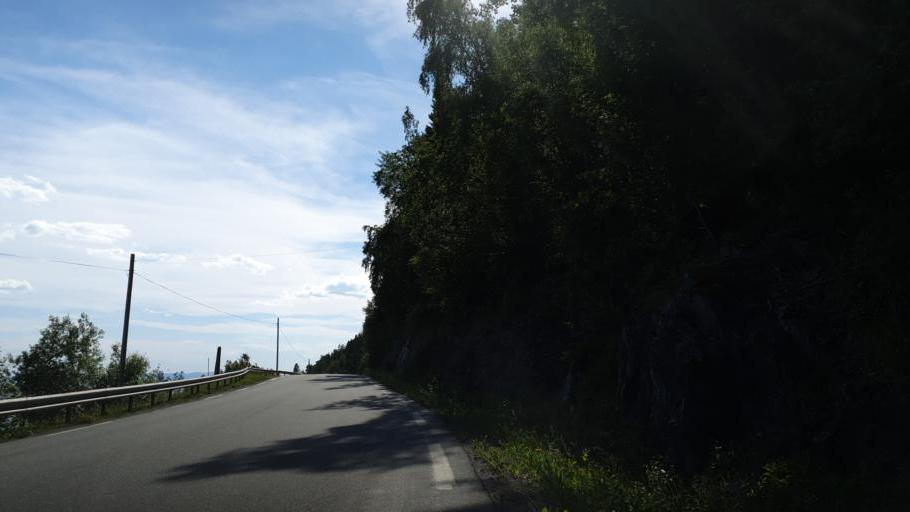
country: NO
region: Nord-Trondelag
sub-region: Leksvik
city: Leksvik
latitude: 63.6439
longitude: 10.5953
